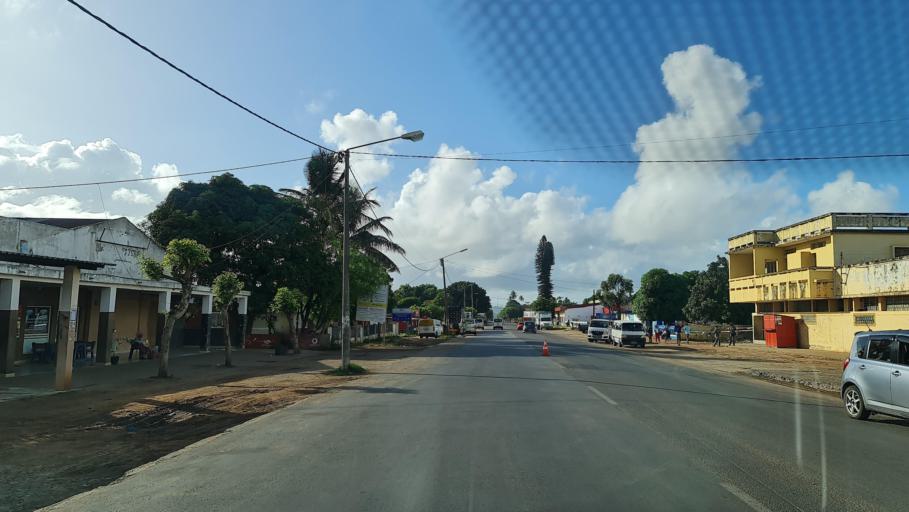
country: MZ
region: Gaza
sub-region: Xai-Xai District
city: Xai-Xai
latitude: -25.0298
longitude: 33.6329
